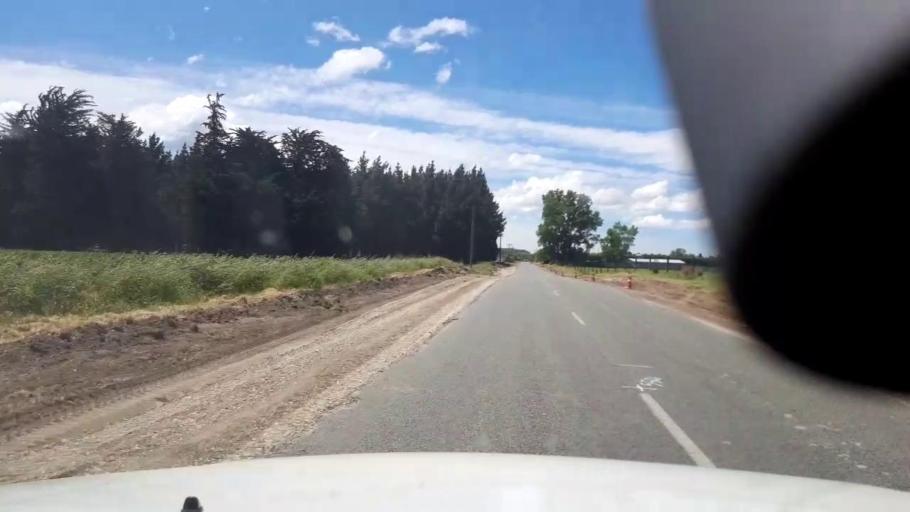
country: NZ
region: Canterbury
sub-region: Timaru District
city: Pleasant Point
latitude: -44.2767
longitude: 171.2504
